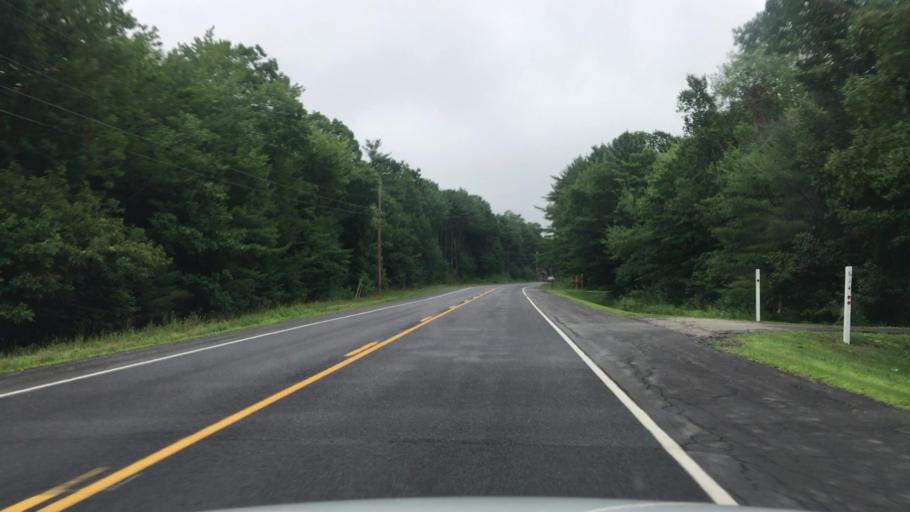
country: US
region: Maine
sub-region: Knox County
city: Union
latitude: 44.2142
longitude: -69.2363
